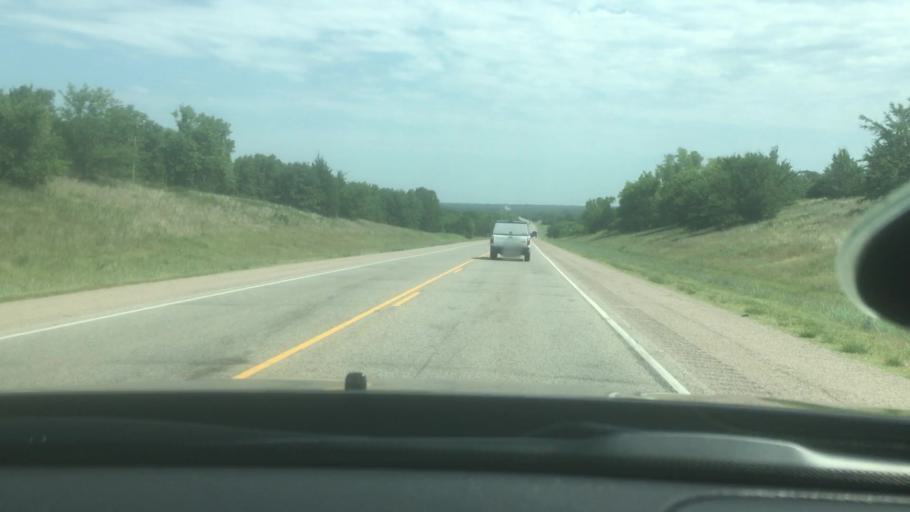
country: US
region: Oklahoma
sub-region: Seminole County
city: Maud
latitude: 35.0596
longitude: -96.9315
